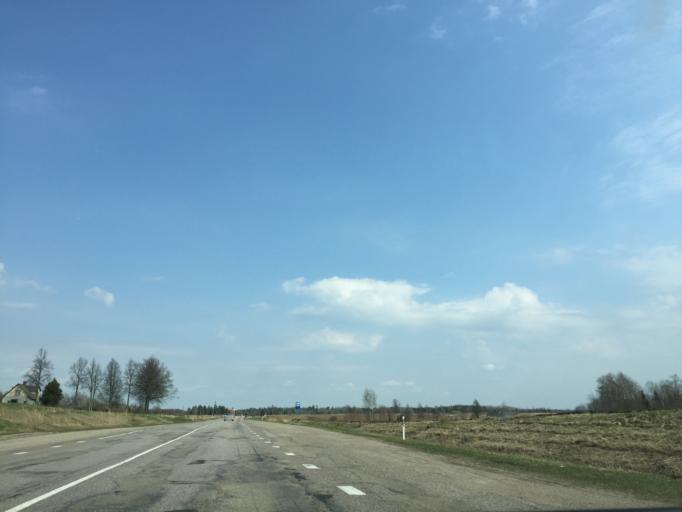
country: LV
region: Apes Novads
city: Ape
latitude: 57.4913
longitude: 26.5711
